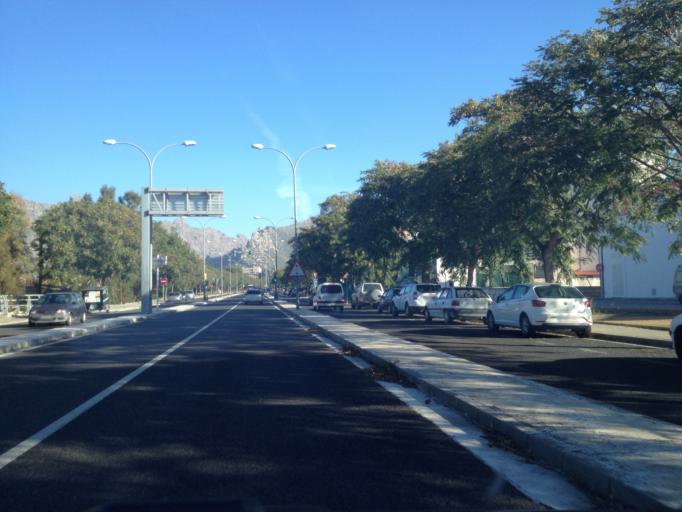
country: ES
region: Balearic Islands
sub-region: Illes Balears
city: Pollenca
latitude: 39.9051
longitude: 3.0756
